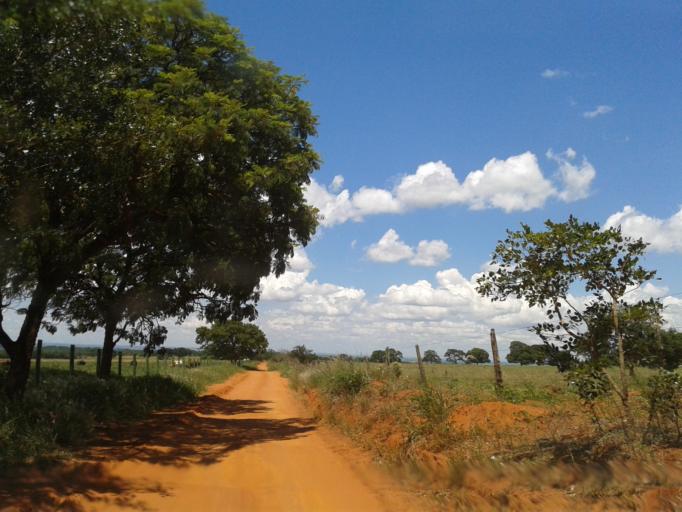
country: BR
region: Minas Gerais
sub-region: Centralina
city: Centralina
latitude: -18.6979
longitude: -49.1582
